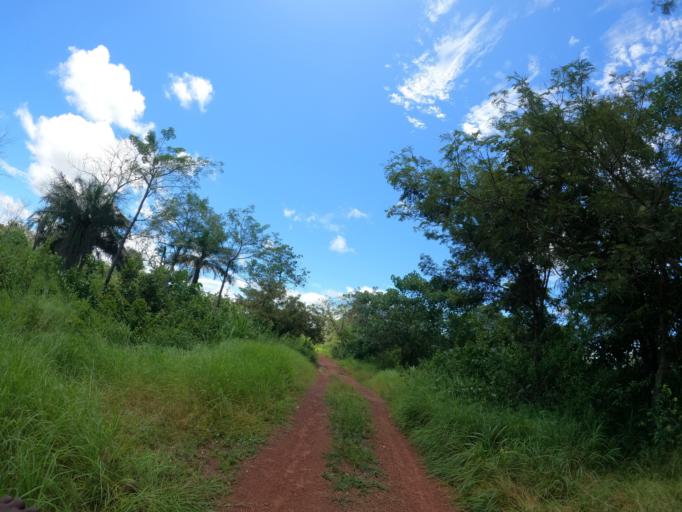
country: SL
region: Northern Province
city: Makeni
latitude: 9.0761
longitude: -12.2724
